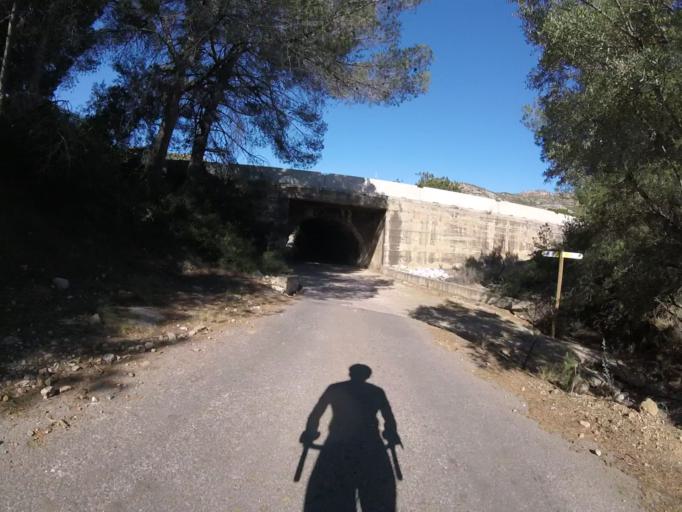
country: ES
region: Valencia
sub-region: Provincia de Castello
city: Orpesa/Oropesa del Mar
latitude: 40.0745
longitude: 0.1111
